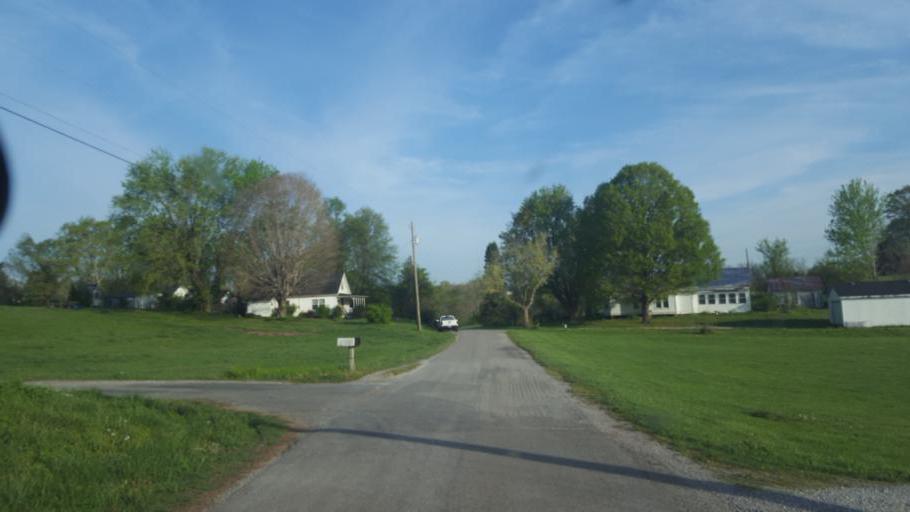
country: US
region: Kentucky
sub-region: Hart County
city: Munfordville
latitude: 37.2621
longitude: -85.8873
